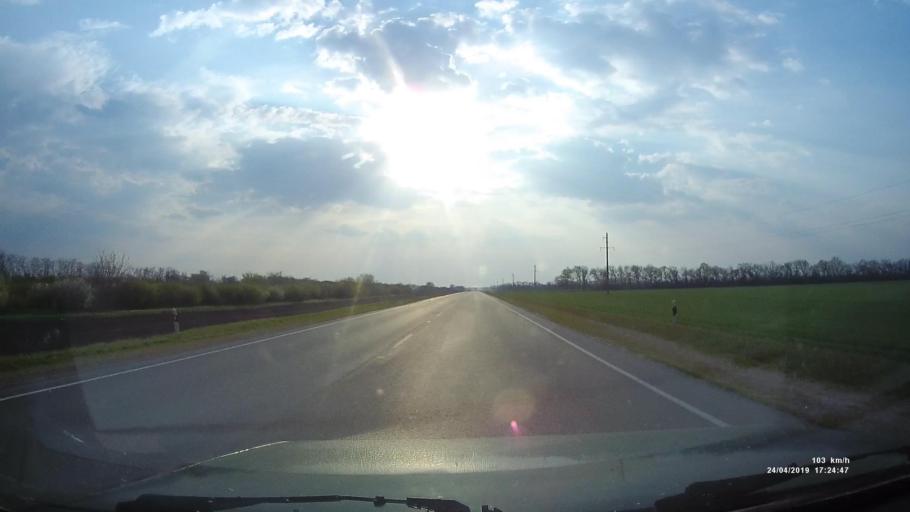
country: RU
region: Rostov
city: Gigant
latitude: 46.5244
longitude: 41.2544
